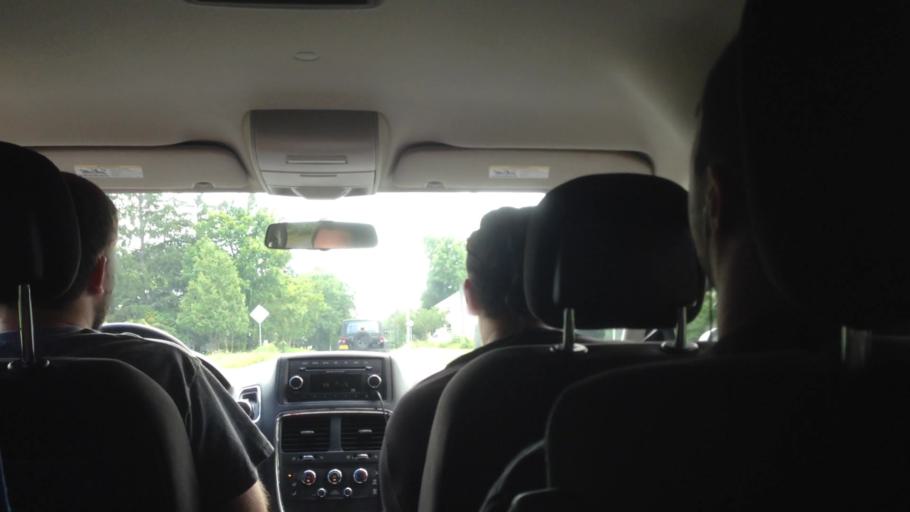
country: US
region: New York
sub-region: Dutchess County
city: Tivoli
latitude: 42.0561
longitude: -73.8985
